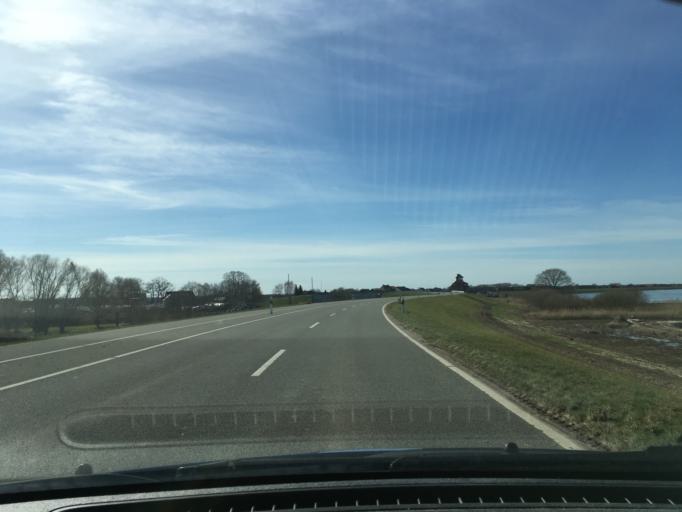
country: DE
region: Lower Saxony
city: Winsen
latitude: 53.3940
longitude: 10.1848
